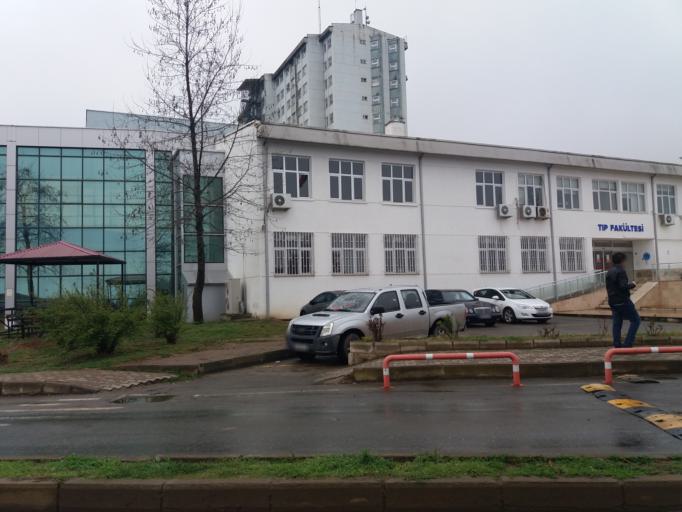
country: TR
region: Trabzon
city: Trabzon
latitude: 40.9931
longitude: 39.7710
